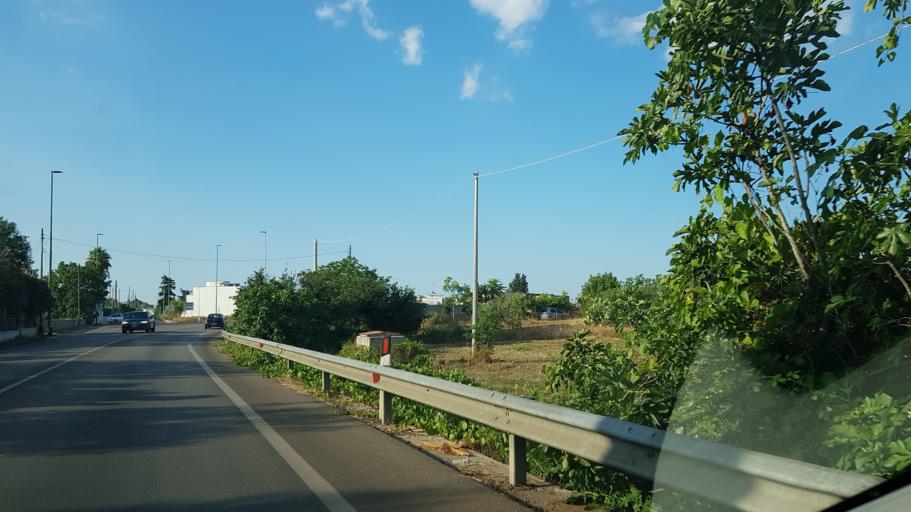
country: IT
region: Apulia
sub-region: Provincia di Lecce
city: Montesano Salentino
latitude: 39.9673
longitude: 18.3231
